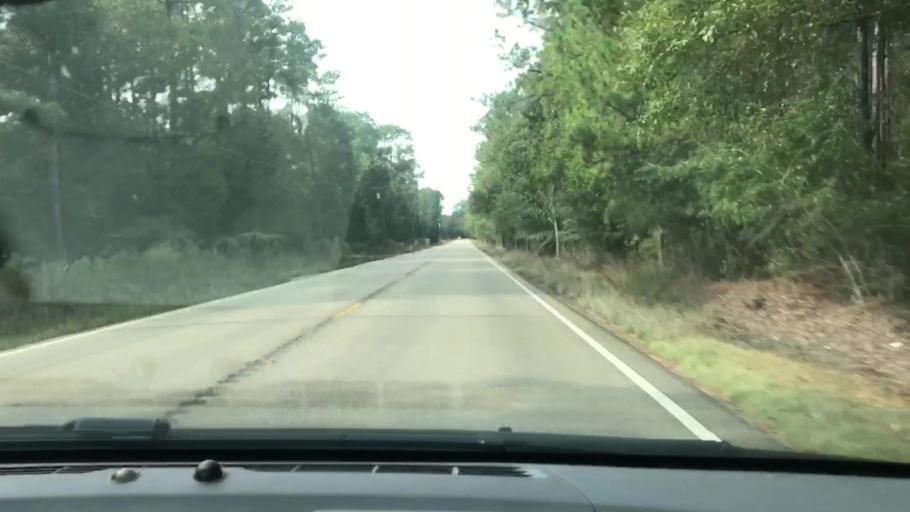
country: US
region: Louisiana
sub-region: Saint Tammany Parish
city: Abita Springs
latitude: 30.5051
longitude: -89.9837
